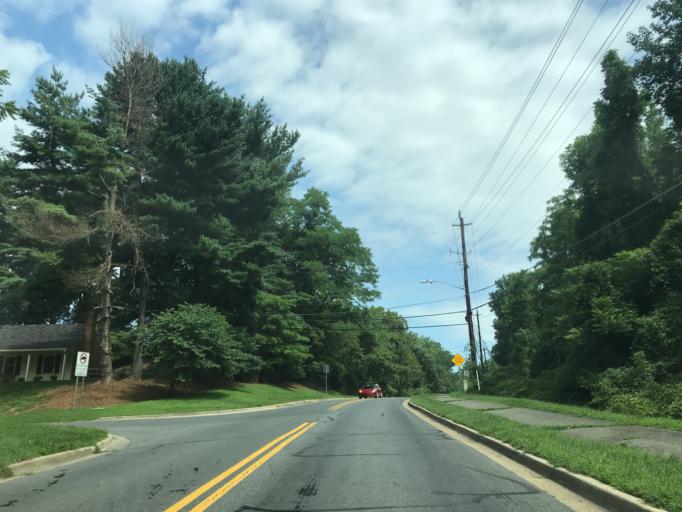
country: US
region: Maryland
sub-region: Montgomery County
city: Cabin John
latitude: 38.9875
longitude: -77.1602
